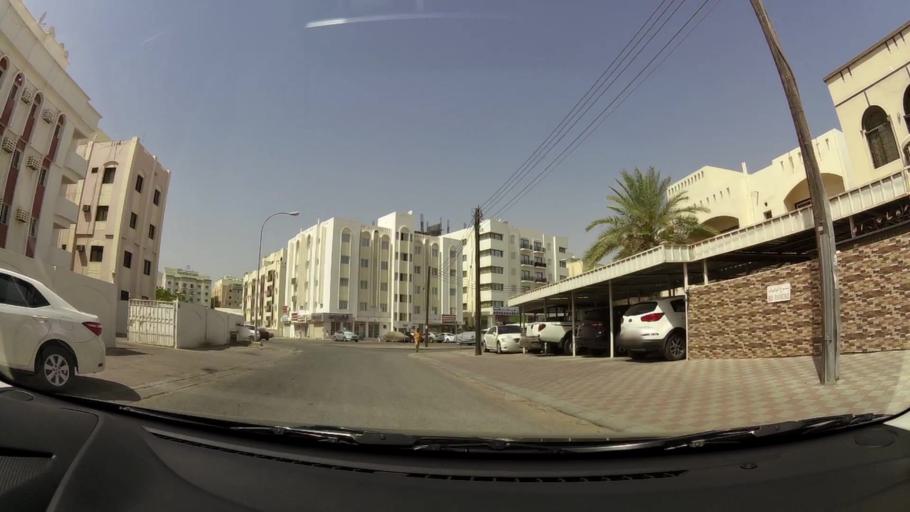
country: OM
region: Muhafazat Masqat
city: Bawshar
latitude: 23.5883
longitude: 58.4254
